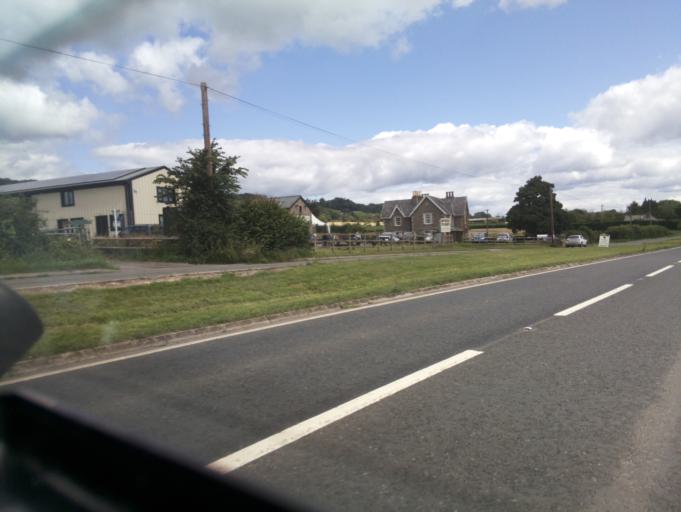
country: GB
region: Wales
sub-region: Monmouthshire
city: Chepstow
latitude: 51.6677
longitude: -2.6298
